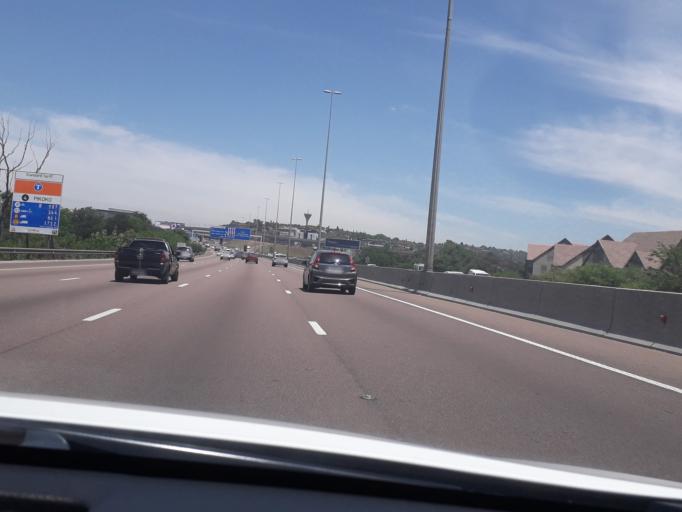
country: ZA
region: Gauteng
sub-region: City of Tshwane Metropolitan Municipality
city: Centurion
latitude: -25.8637
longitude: 28.2013
